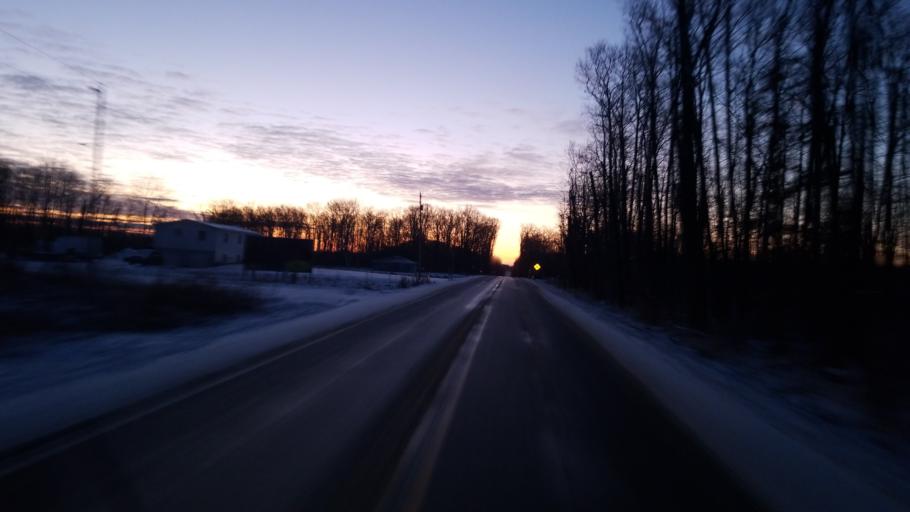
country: US
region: Pennsylvania
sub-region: Clarion County
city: Knox
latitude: 41.2733
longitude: -79.5710
